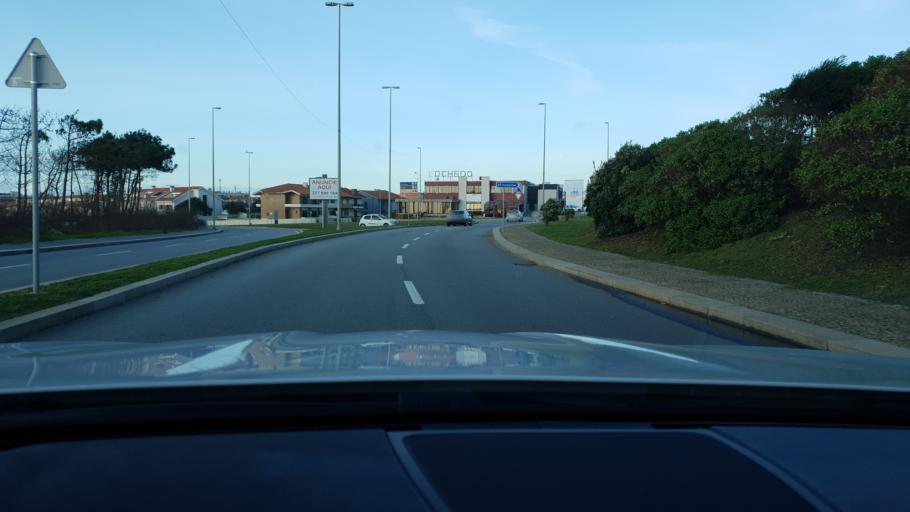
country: PT
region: Porto
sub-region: Matosinhos
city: Santa Cruz do Bispo
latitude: 41.2188
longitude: -8.7126
